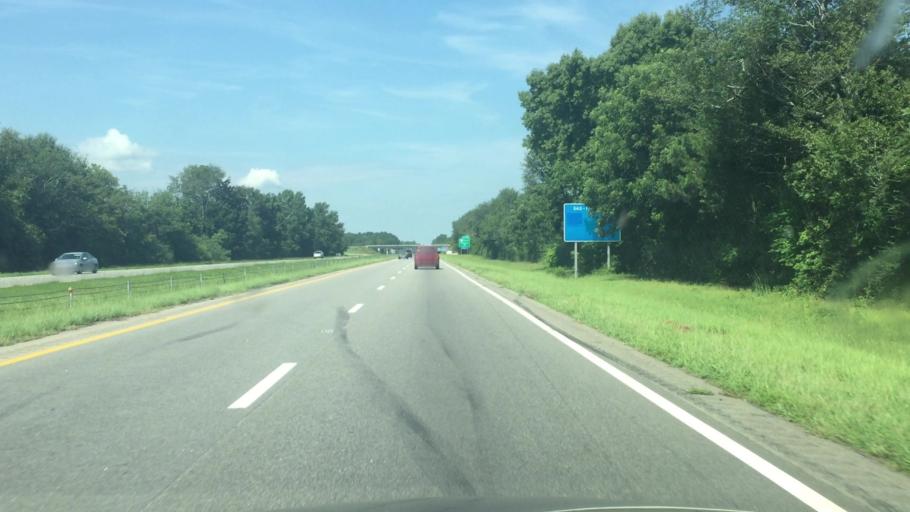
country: US
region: North Carolina
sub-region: Scotland County
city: Laurinburg
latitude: 34.7551
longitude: -79.4521
